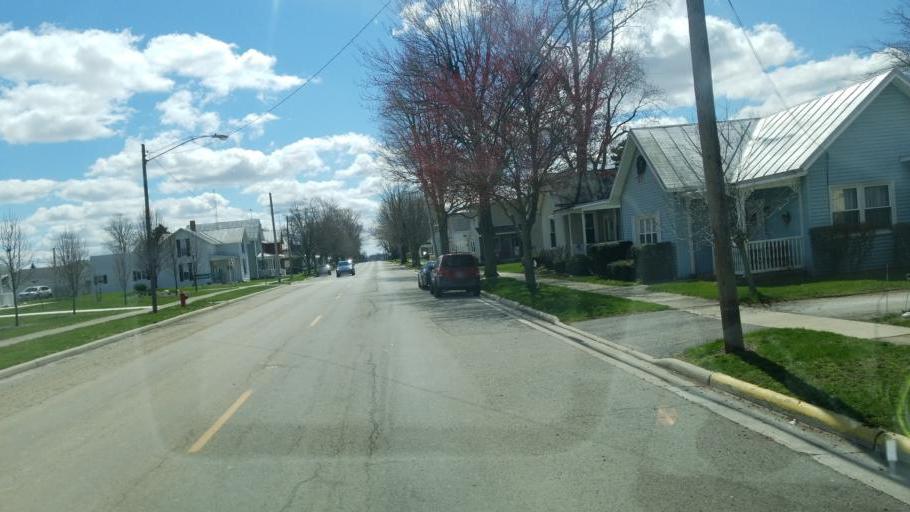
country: US
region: Ohio
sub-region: Hancock County
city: Arlington
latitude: 40.8963
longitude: -83.5568
